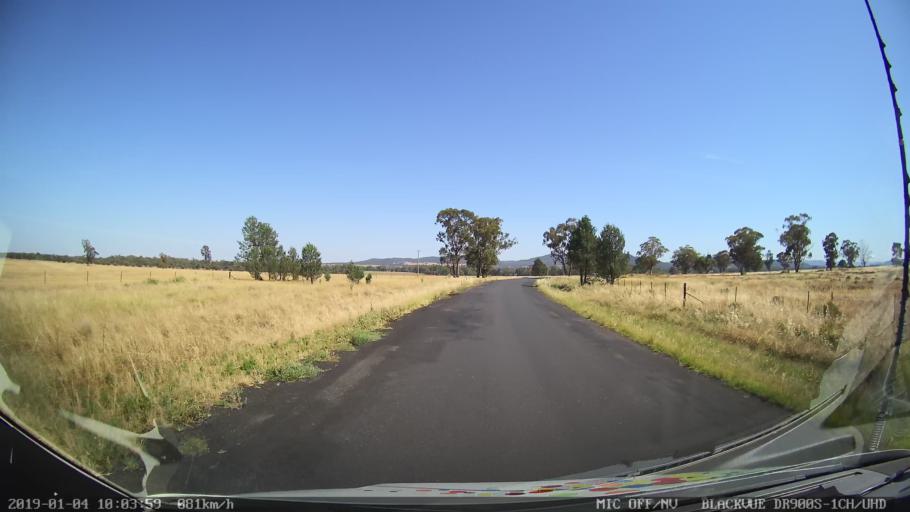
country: AU
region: New South Wales
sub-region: Cabonne
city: Canowindra
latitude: -33.4574
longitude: 148.3616
